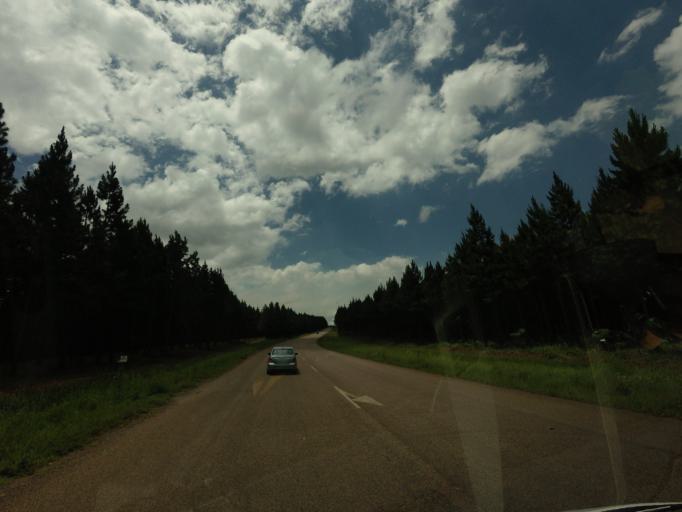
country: ZA
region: Mpumalanga
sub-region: Ehlanzeni District
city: Graksop
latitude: -25.0315
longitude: 30.8207
